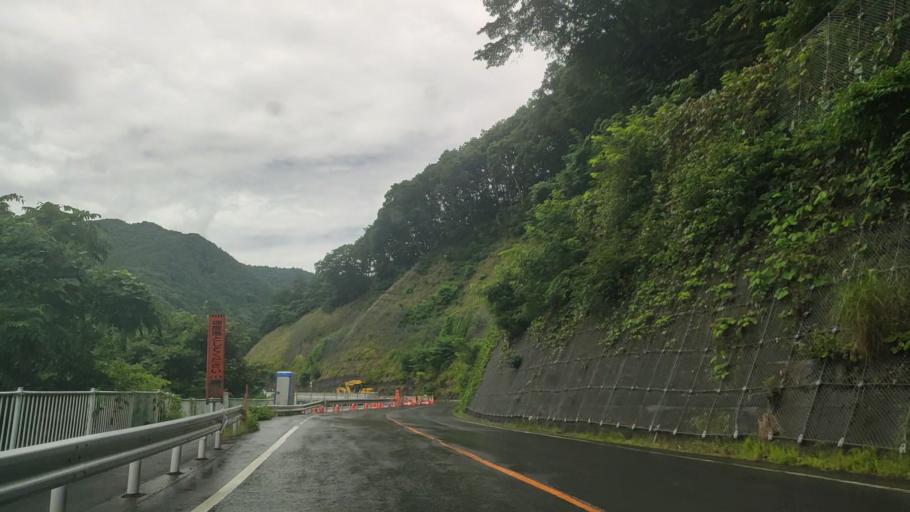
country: JP
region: Gunma
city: Numata
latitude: 36.7675
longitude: 139.2278
